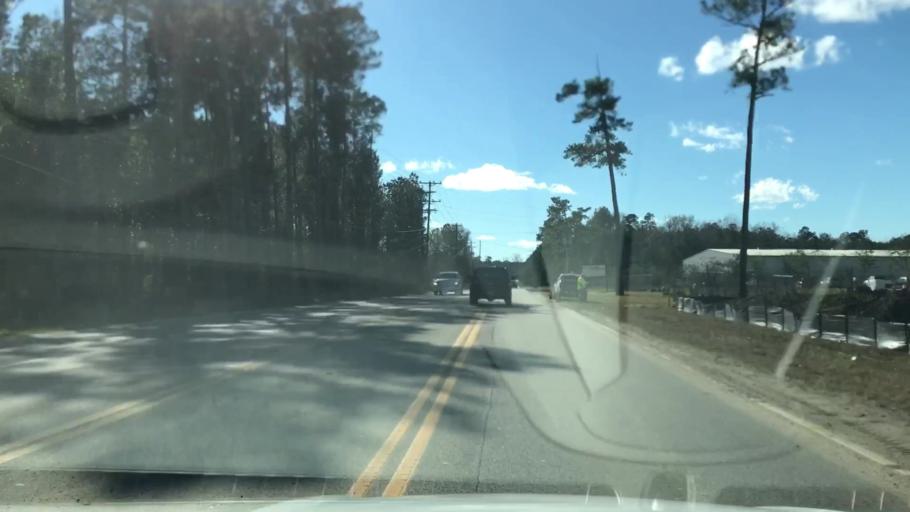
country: US
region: South Carolina
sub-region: Dorchester County
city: Summerville
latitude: 33.0593
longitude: -80.2328
